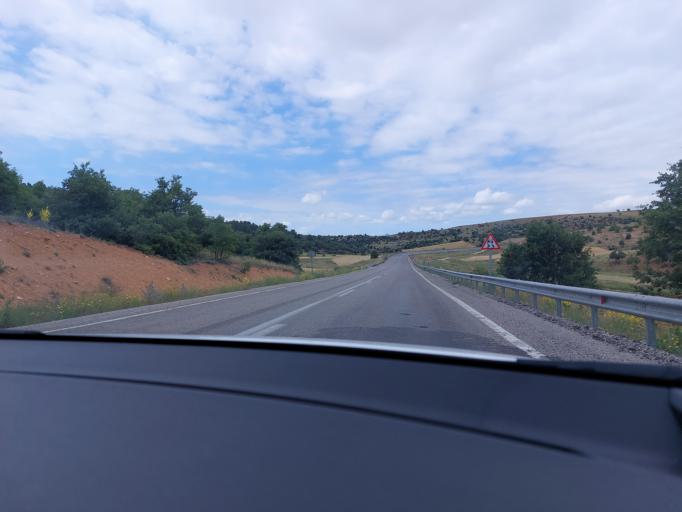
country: TR
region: Konya
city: Doganbey
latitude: 37.8965
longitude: 31.8039
